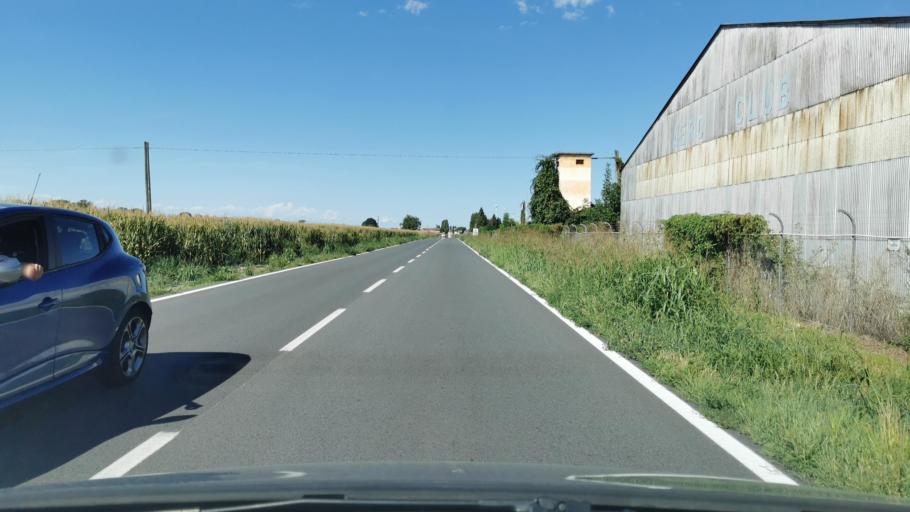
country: IT
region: Piedmont
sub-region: Provincia di Cuneo
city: Vottignasco
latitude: 44.5418
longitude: 7.6135
